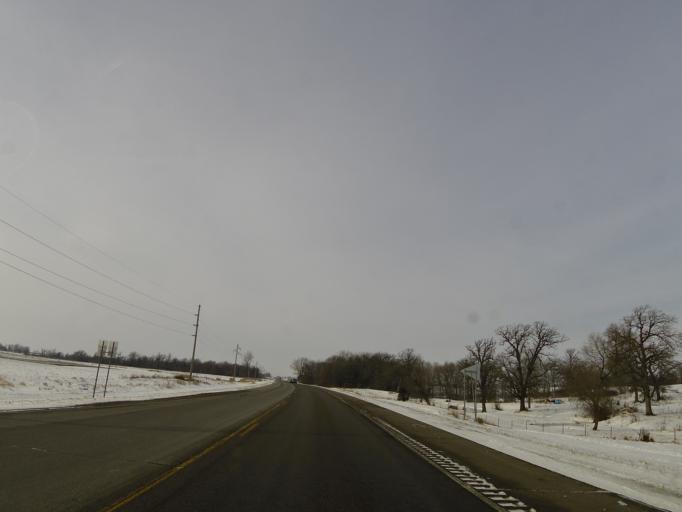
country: US
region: Minnesota
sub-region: Carver County
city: Mayer
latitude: 44.9056
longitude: -93.8917
